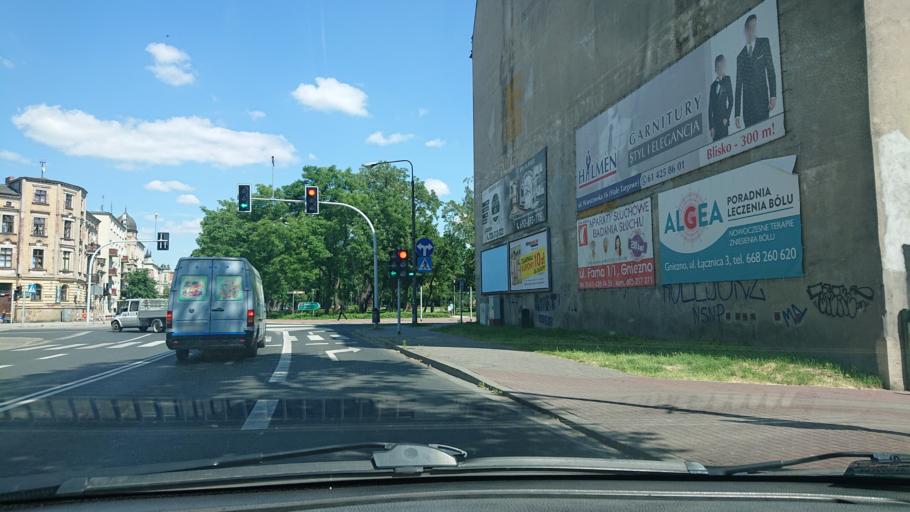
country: PL
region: Greater Poland Voivodeship
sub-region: Powiat gnieznienski
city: Gniezno
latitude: 52.5306
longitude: 17.5983
